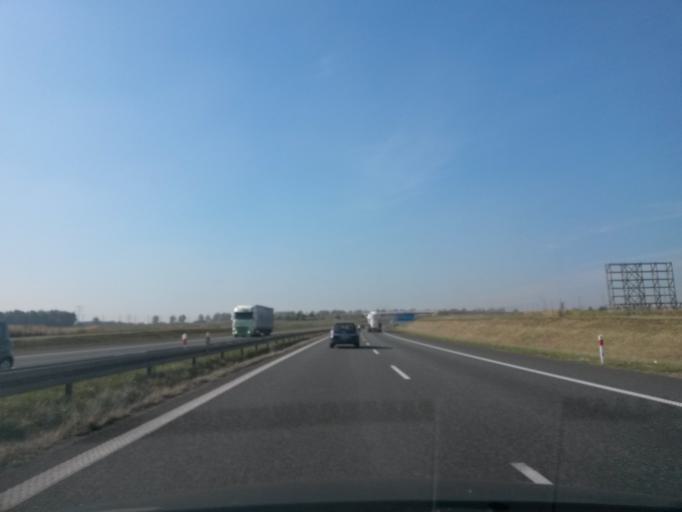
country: PL
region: Silesian Voivodeship
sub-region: Powiat gliwicki
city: Zernica
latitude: 50.2662
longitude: 18.5931
